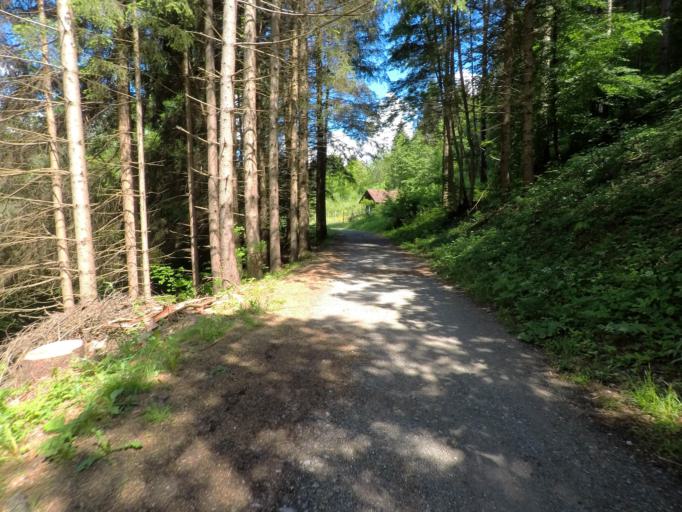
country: IT
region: Friuli Venezia Giulia
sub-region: Provincia di Udine
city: Ovaro
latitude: 46.4775
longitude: 12.8715
